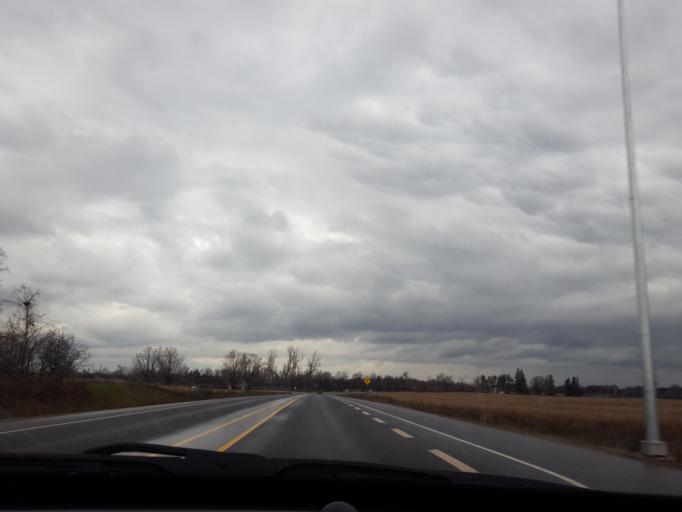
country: CA
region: Ontario
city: Pickering
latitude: 43.9243
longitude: -79.1052
